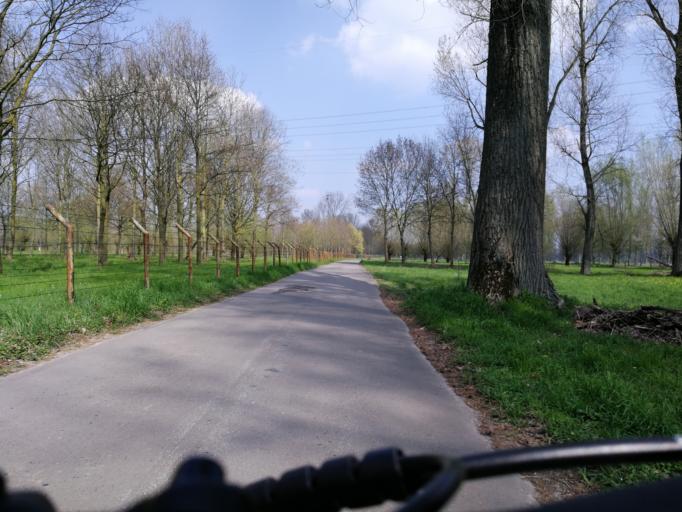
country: DE
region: North Rhine-Westphalia
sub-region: Regierungsbezirk Dusseldorf
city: Dormagen
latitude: 51.1514
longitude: 6.8341
